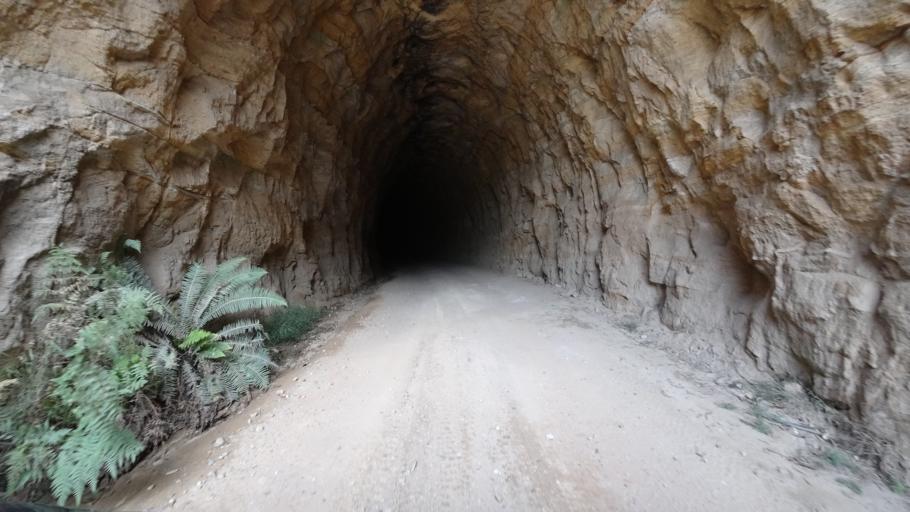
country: AU
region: New South Wales
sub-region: Lithgow
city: Lithgow
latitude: -33.2493
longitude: 150.2205
